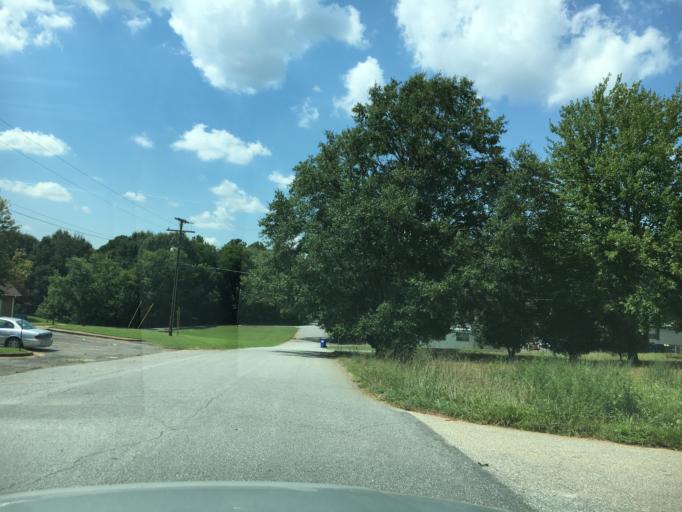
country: US
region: South Carolina
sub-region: Spartanburg County
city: Duncan
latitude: 34.9309
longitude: -82.1310
